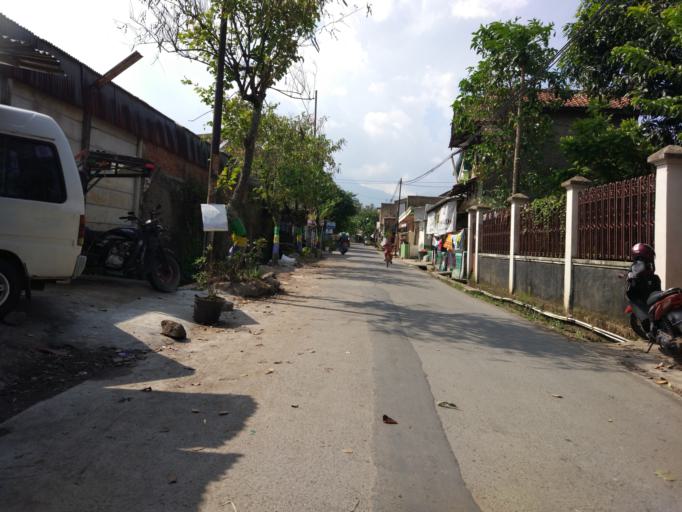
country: ID
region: West Java
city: Cileunyi
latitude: -6.9282
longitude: 107.7047
